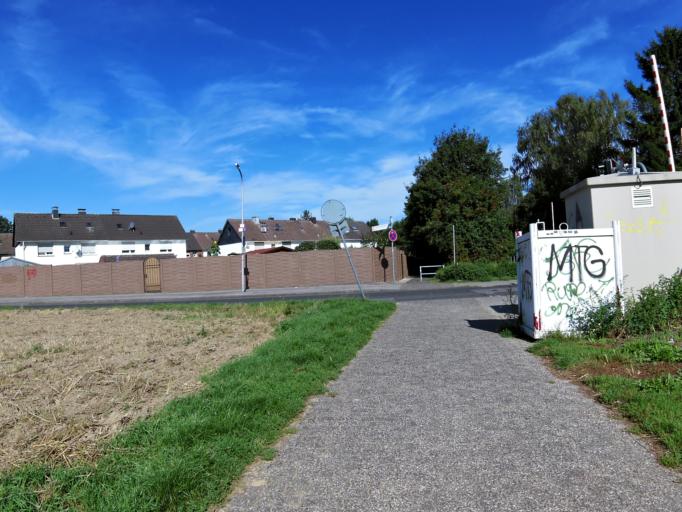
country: DE
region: North Rhine-Westphalia
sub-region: Regierungsbezirk Koln
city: Alsdorf
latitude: 50.8559
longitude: 6.1967
